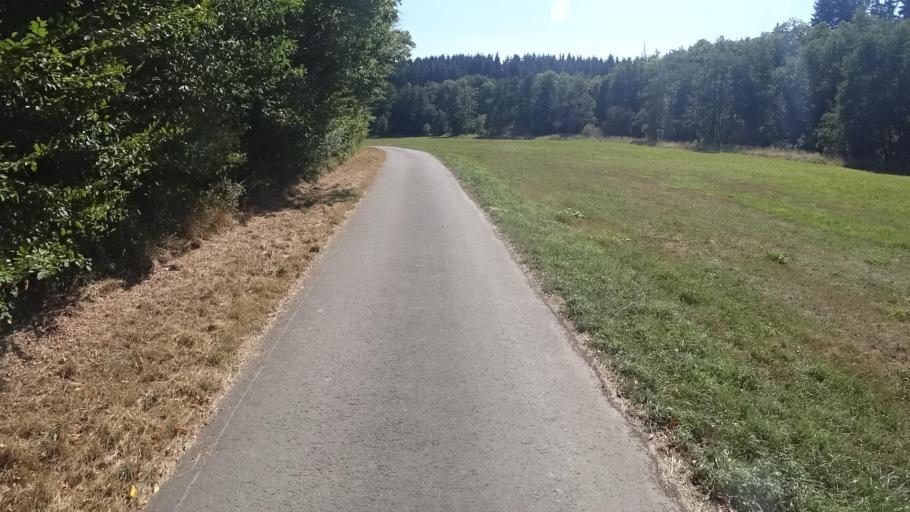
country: DE
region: Rheinland-Pfalz
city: Ravengiersburg
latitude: 49.9290
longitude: 7.4807
